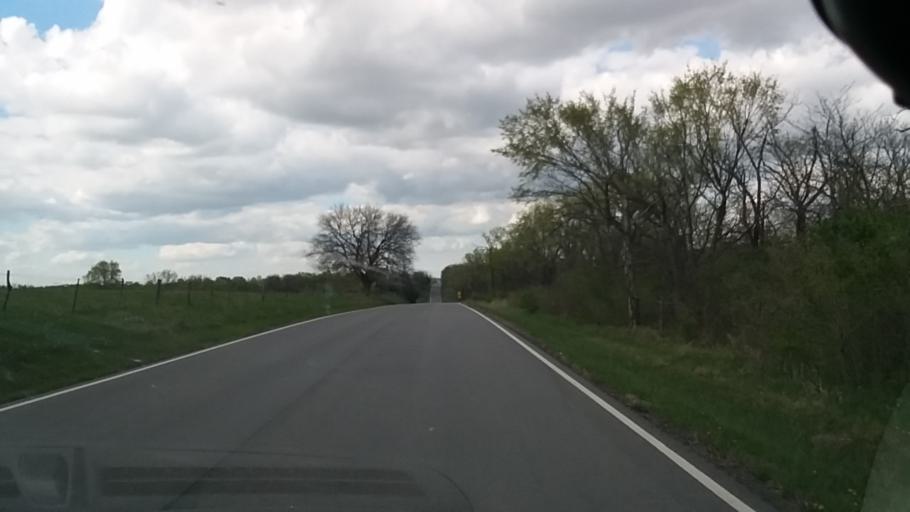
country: US
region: Kansas
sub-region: Douglas County
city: Lawrence
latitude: 38.8870
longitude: -95.2418
